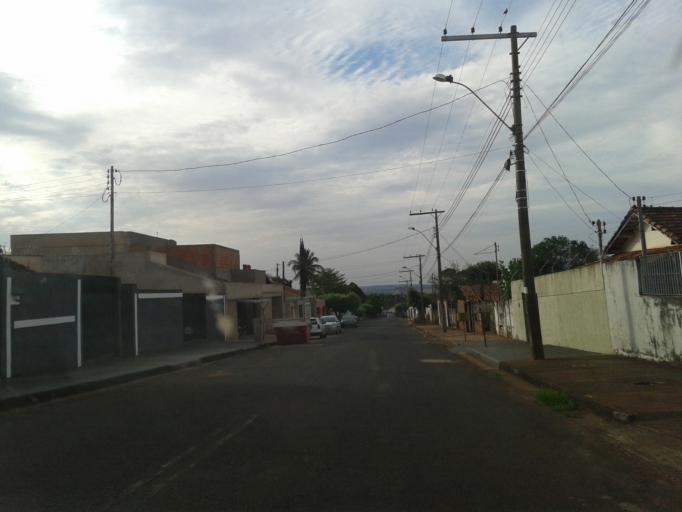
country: BR
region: Minas Gerais
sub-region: Ituiutaba
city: Ituiutaba
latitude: -18.9901
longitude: -49.4523
